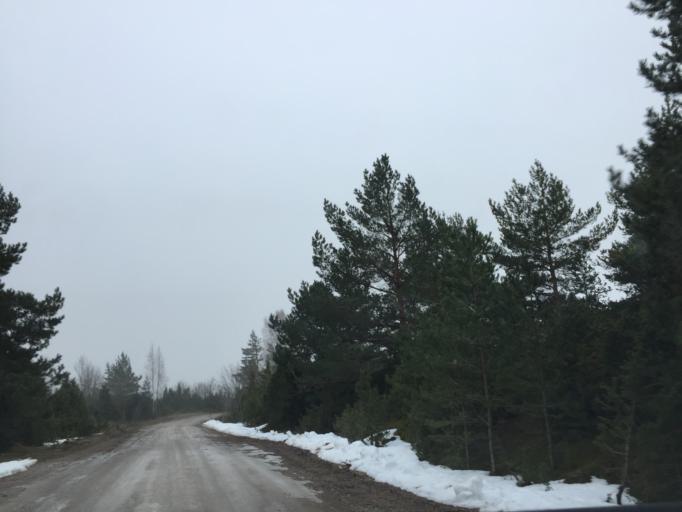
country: EE
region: Saare
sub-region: Kuressaare linn
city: Kuressaare
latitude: 58.4950
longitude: 21.9840
